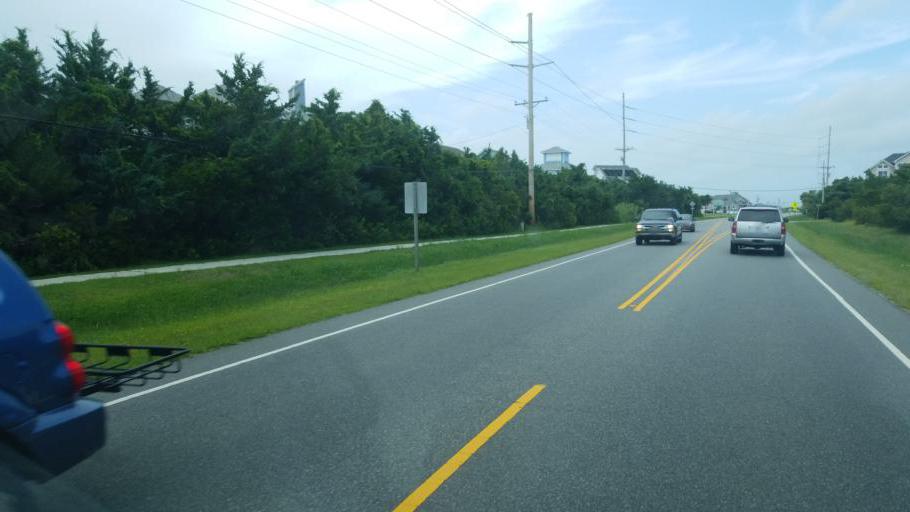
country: US
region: North Carolina
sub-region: Dare County
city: Buxton
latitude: 35.3295
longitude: -75.5077
